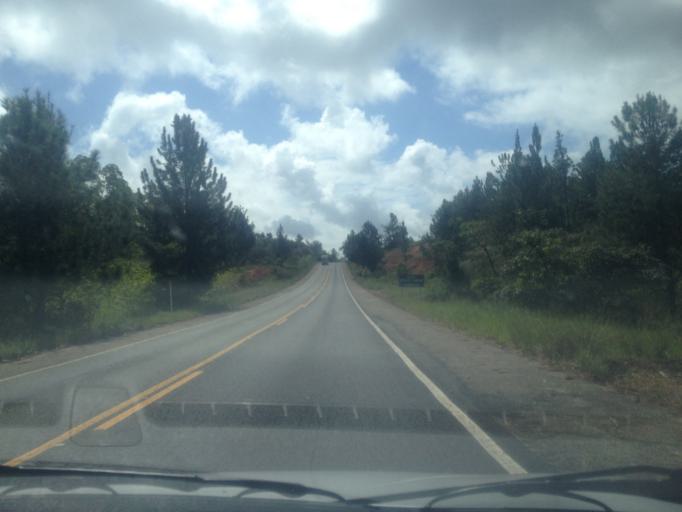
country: BR
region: Bahia
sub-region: Conde
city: Conde
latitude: -12.0063
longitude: -37.6856
